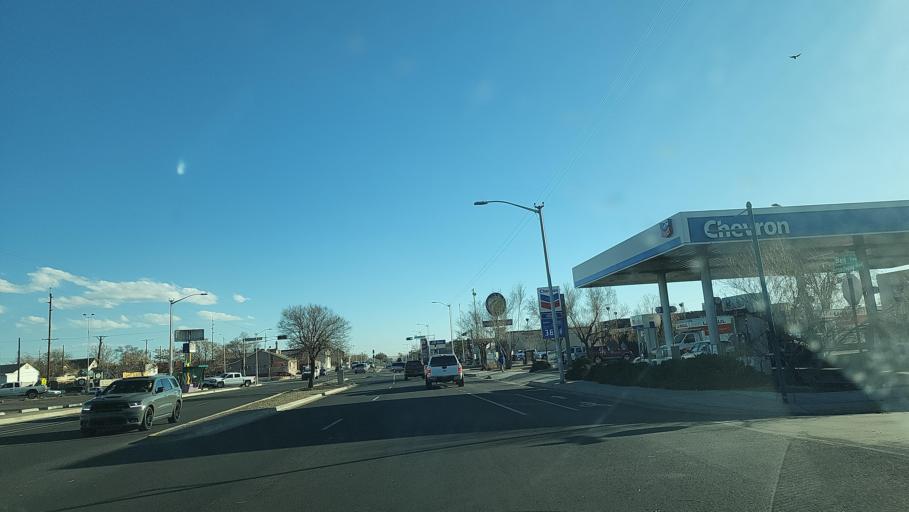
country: US
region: New Mexico
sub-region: Bernalillo County
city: Albuquerque
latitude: 35.0707
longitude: -106.6457
